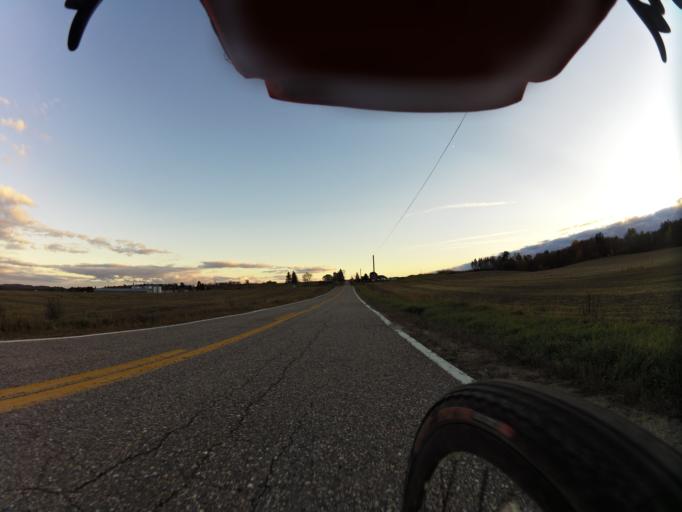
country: CA
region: Quebec
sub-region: Outaouais
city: Shawville
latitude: 45.6151
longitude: -76.3060
